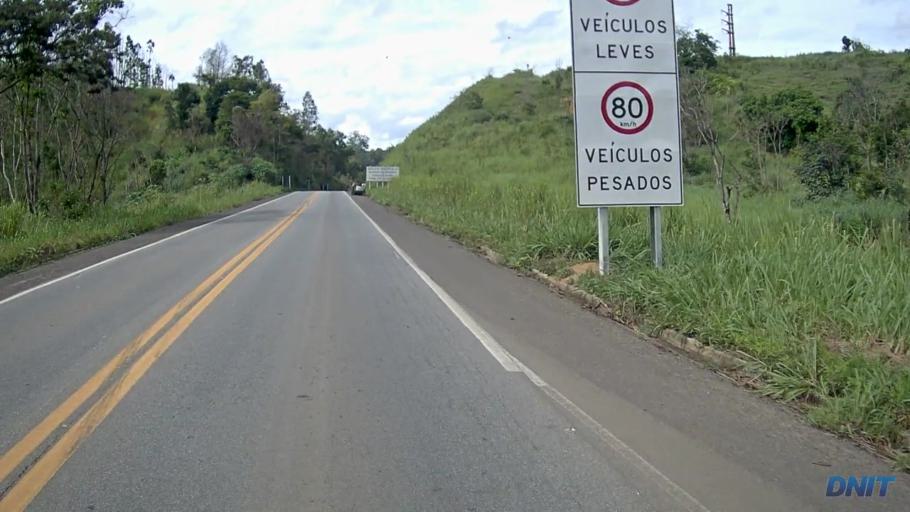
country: BR
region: Minas Gerais
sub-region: Ipaba
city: Ipaba
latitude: -19.3350
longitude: -42.4245
